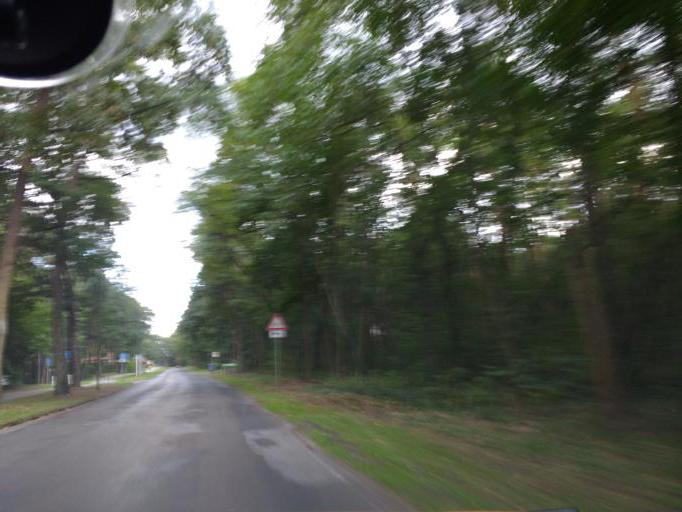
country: DE
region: Brandenburg
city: Bad Saarow
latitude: 52.2820
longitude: 14.0384
